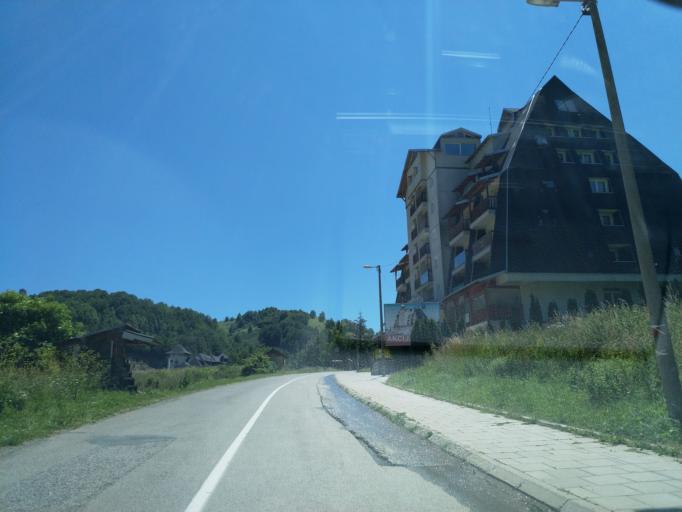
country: XK
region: Mitrovica
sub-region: Komuna e Leposaviqit
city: Leposaviq
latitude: 43.2889
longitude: 20.8800
